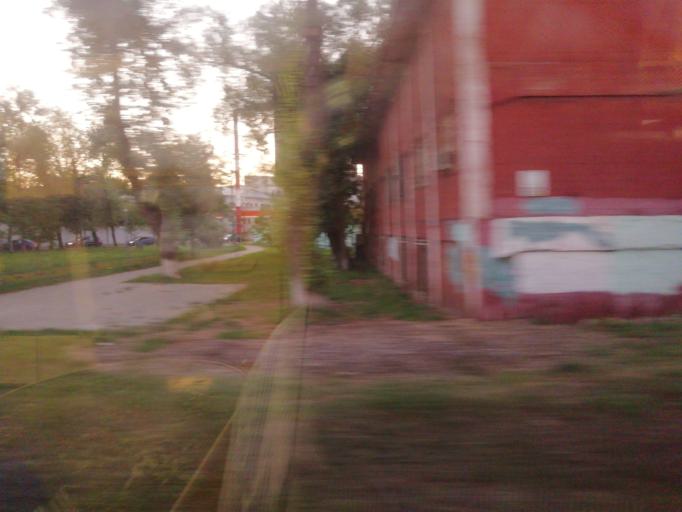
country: RU
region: Moscow
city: Mar'ina Roshcha
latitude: 55.7991
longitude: 37.5973
